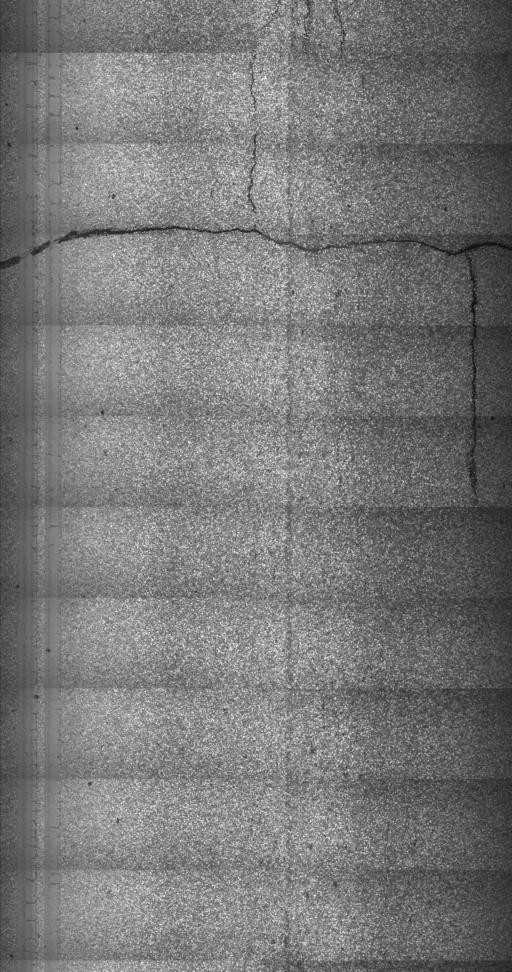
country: US
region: Vermont
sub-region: Rutland County
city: Fair Haven
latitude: 43.5996
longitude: -73.2721
